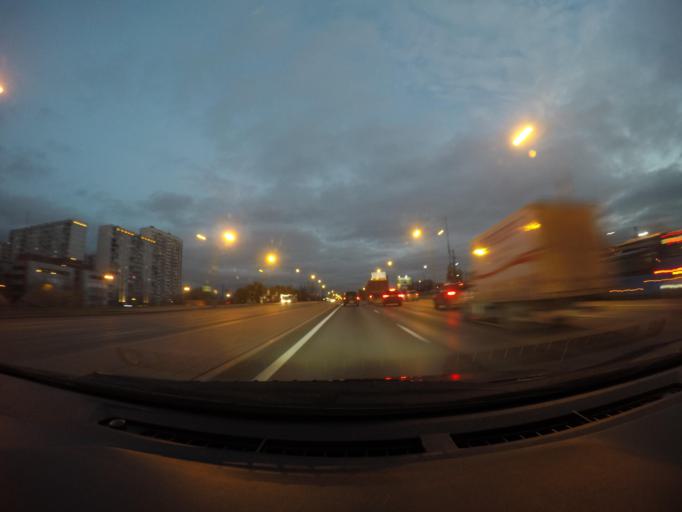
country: RU
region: Moskovskaya
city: Kur'yanovo
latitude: 55.6371
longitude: 37.6934
